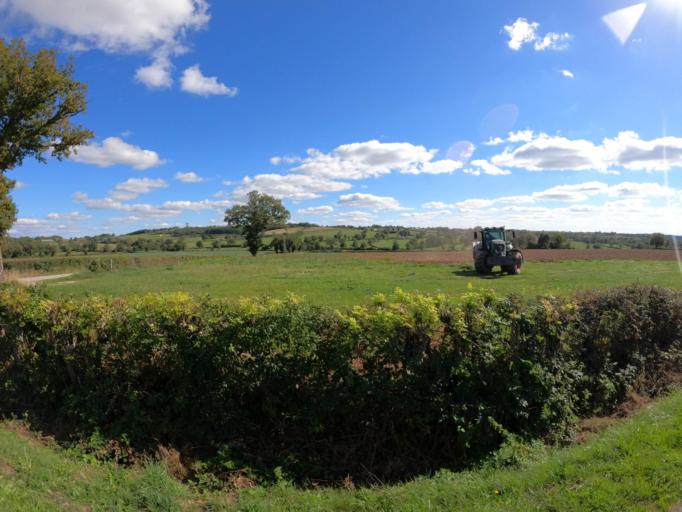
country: FR
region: Auvergne
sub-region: Departement de l'Allier
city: Buxieres-les-Mines
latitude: 46.4035
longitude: 3.0293
